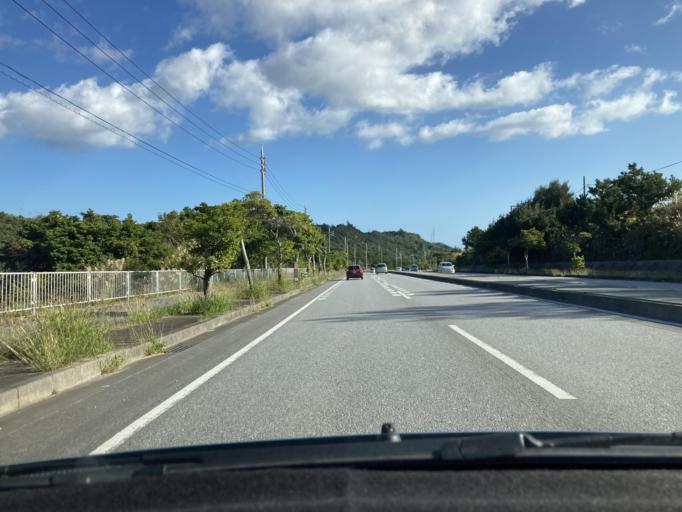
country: JP
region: Okinawa
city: Ishikawa
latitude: 26.4021
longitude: 127.8267
